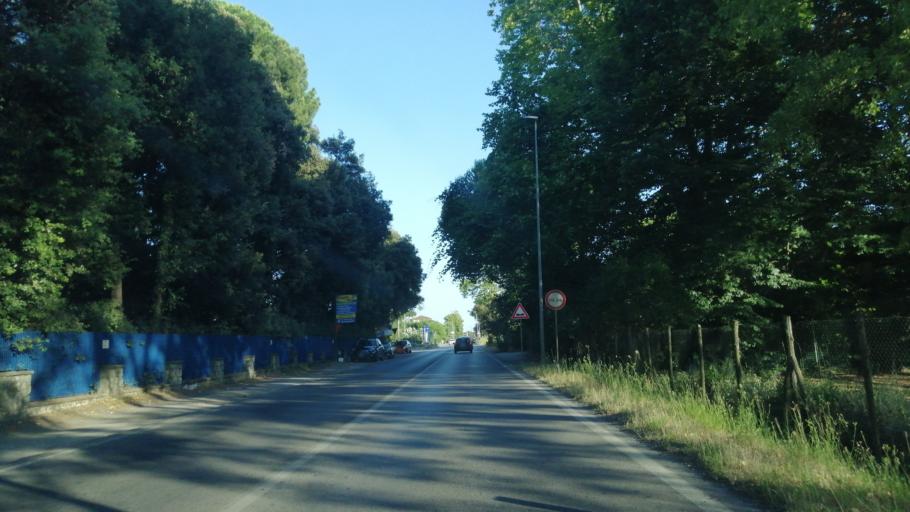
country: IT
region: Tuscany
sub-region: Provincia di Lucca
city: Camaiore
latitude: 43.9133
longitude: 10.2225
